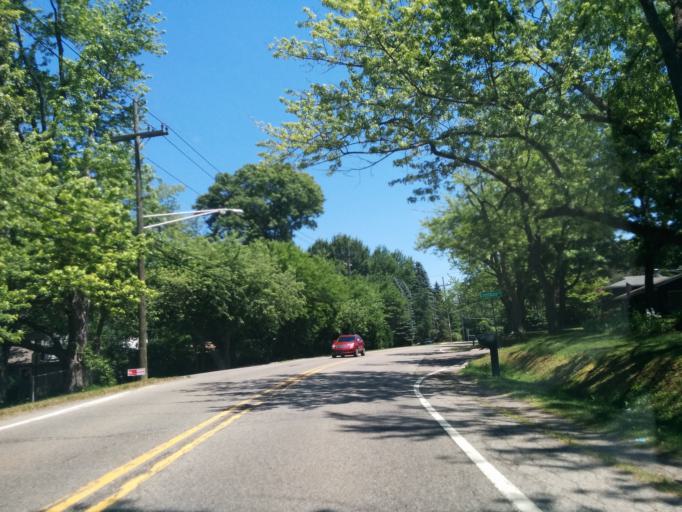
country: US
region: Michigan
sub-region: Oakland County
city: West Bloomfield Township
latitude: 42.5750
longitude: -83.4247
